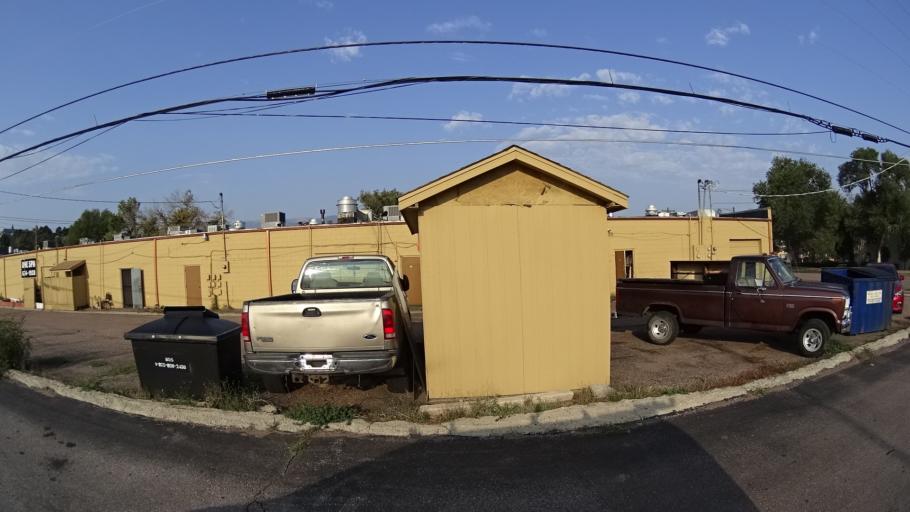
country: US
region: Colorado
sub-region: El Paso County
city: Colorado Springs
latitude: 38.8340
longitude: -104.7895
